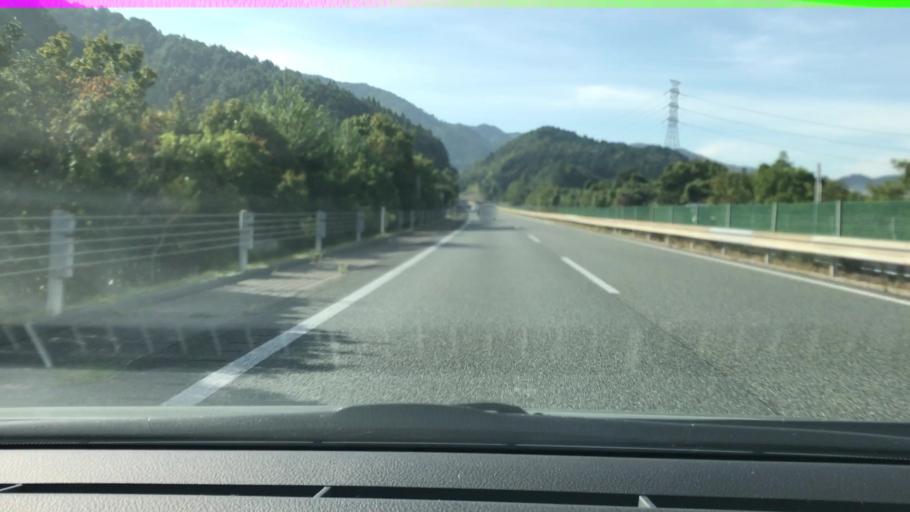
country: JP
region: Hyogo
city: Sasayama
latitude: 35.0465
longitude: 135.1825
